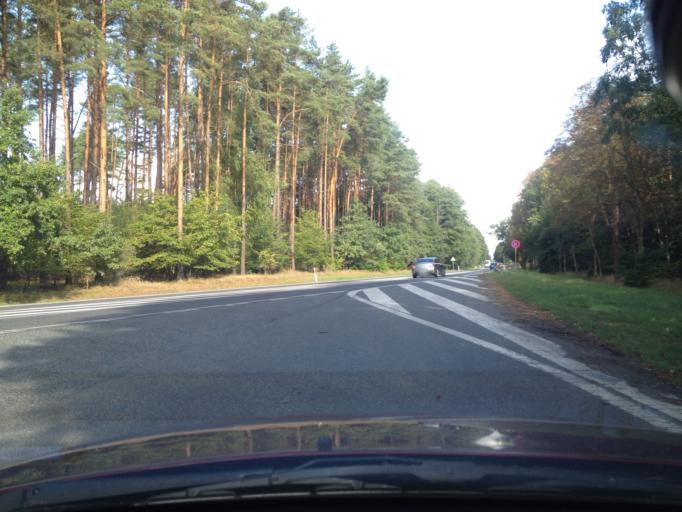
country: PL
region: West Pomeranian Voivodeship
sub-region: Powiat goleniowski
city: Przybiernow
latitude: 53.7703
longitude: 14.7811
